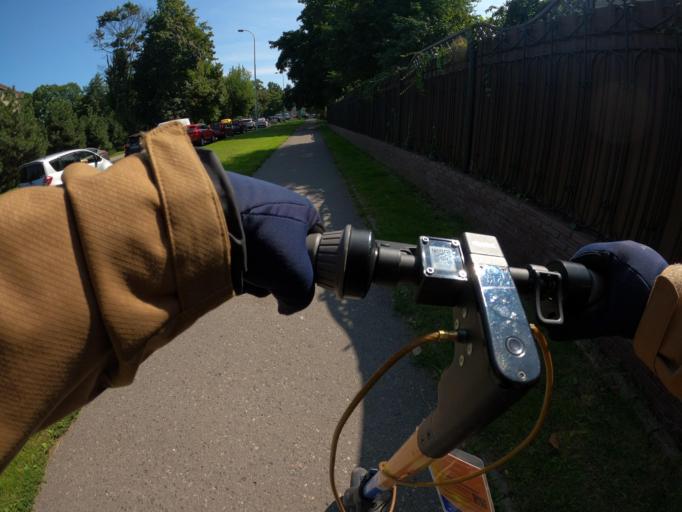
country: RU
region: Kaliningrad
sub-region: Gorod Kaliningrad
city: Kaliningrad
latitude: 54.7342
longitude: 20.5293
